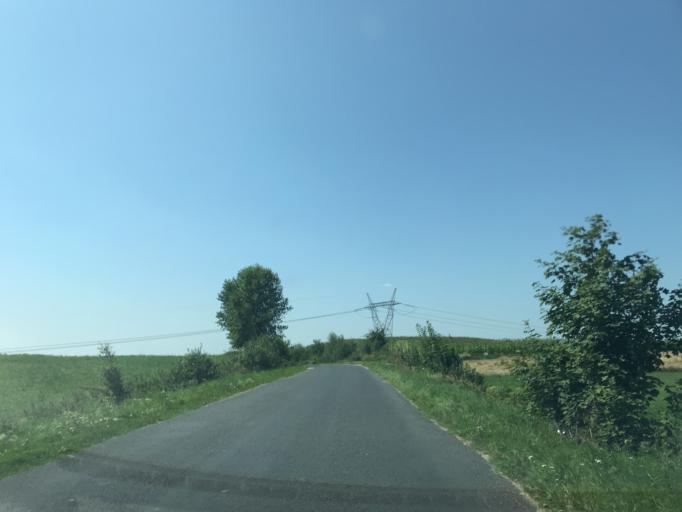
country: PL
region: Kujawsko-Pomorskie
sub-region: Powiat lipnowski
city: Chrostkowo
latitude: 52.9964
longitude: 19.2316
